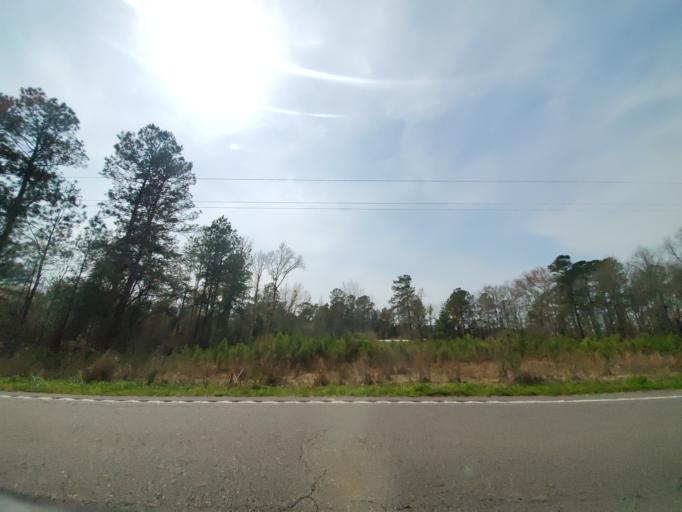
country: US
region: South Carolina
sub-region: Dorchester County
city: Ridgeville
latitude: 32.9712
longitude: -80.3054
